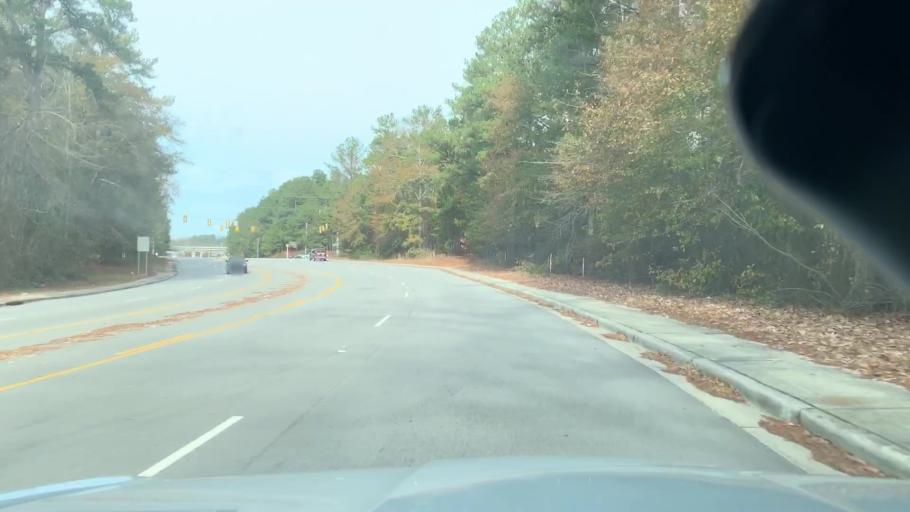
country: US
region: South Carolina
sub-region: Richland County
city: Dentsville
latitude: 34.0677
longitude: -80.9473
